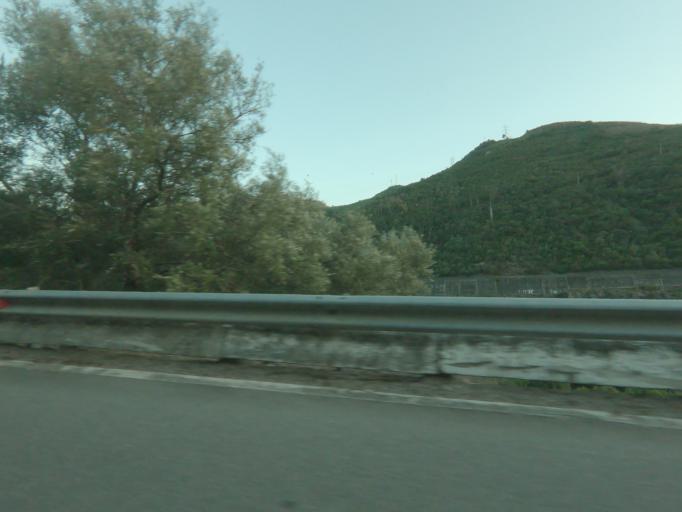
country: PT
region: Vila Real
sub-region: Peso da Regua
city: Peso da Regua
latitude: 41.1489
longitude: -7.7450
